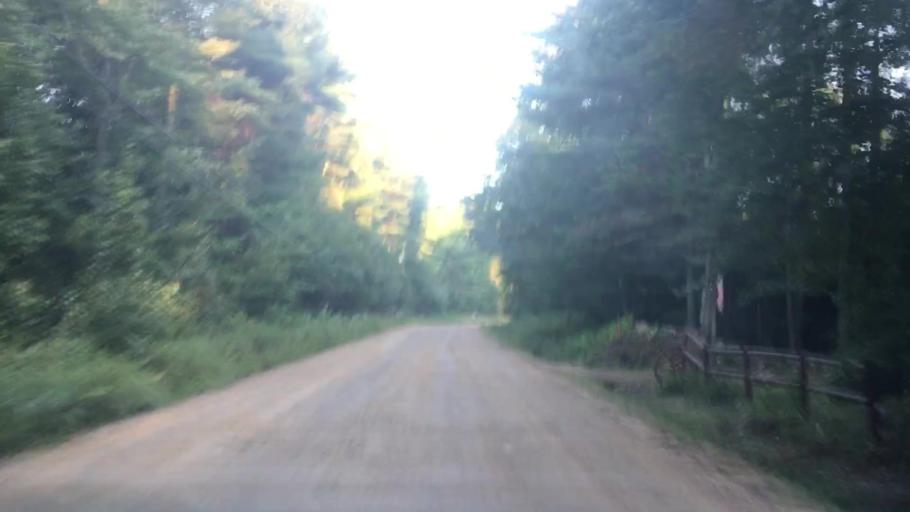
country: US
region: New Hampshire
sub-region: Belknap County
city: Barnstead
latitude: 43.4176
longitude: -71.2886
